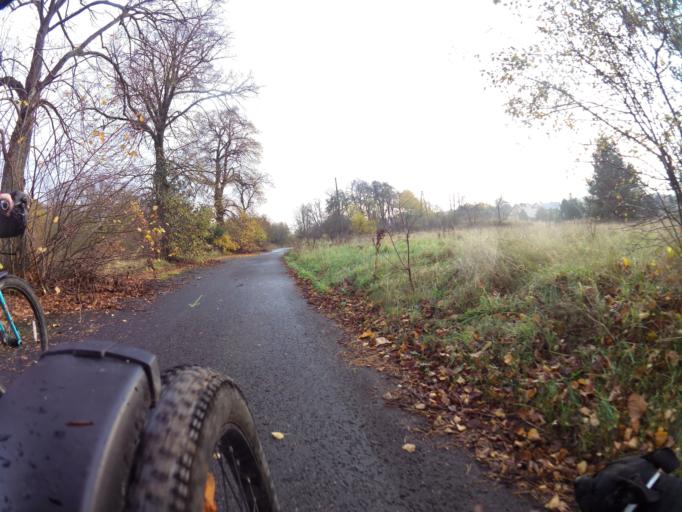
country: PL
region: Pomeranian Voivodeship
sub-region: Powiat wejherowski
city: Gniewino
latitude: 54.7117
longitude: 18.0971
